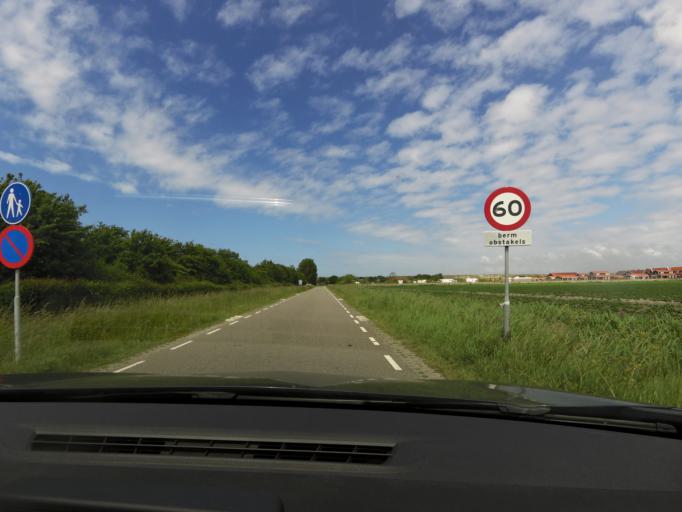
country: NL
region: Zeeland
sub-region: Schouwen-Duiveland
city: Renesse
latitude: 51.7357
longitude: 3.7988
